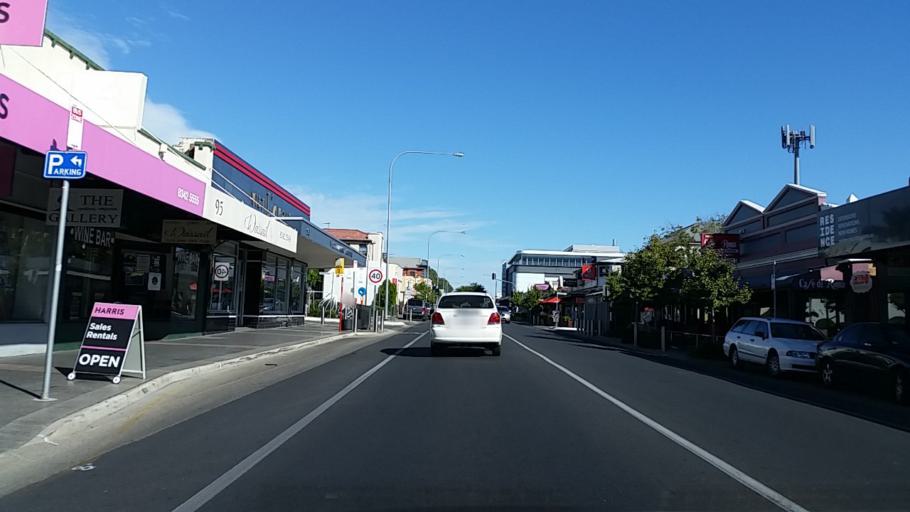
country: AU
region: South Australia
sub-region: Prospect
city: Prospect
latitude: -34.8868
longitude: 138.5940
